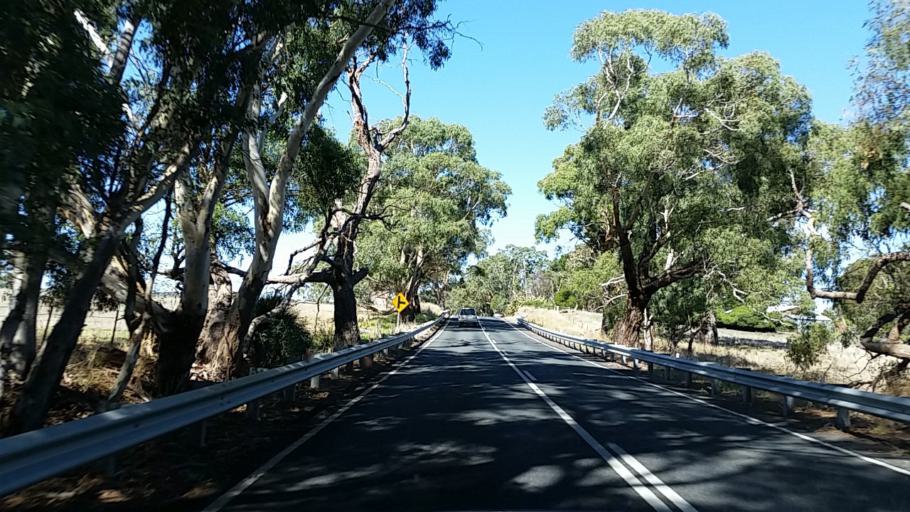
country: AU
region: South Australia
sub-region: Adelaide Hills
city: Birdwood
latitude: -34.7679
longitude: 139.0210
